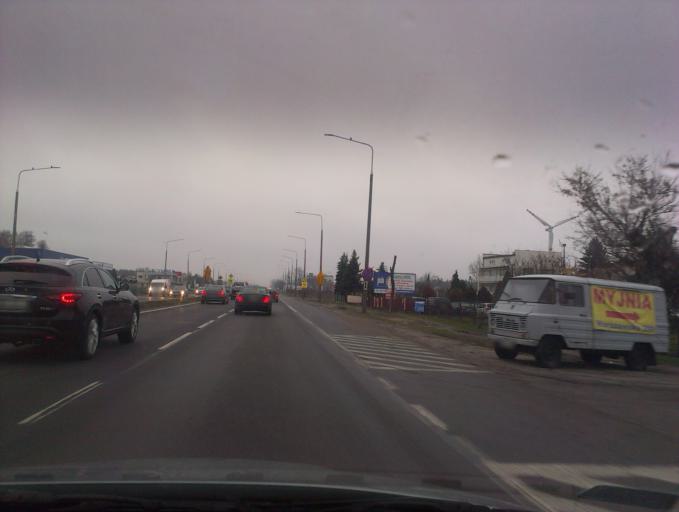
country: PL
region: Masovian Voivodeship
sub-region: Radom
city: Radom
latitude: 51.4441
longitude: 21.1450
